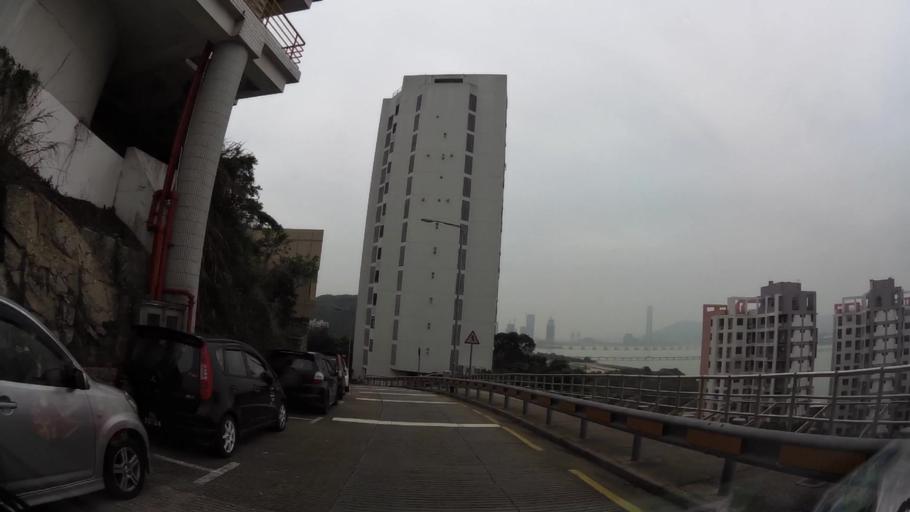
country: MO
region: Macau
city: Macau
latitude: 22.1644
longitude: 113.5572
